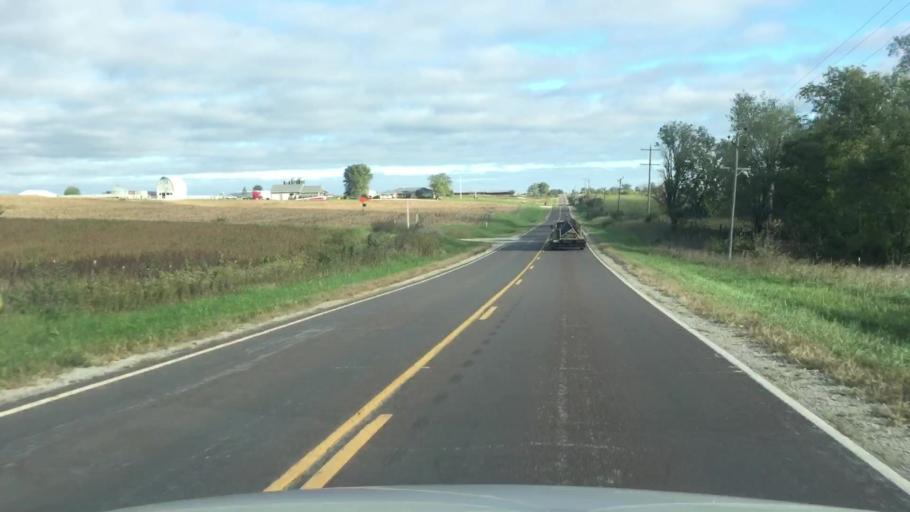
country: US
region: Missouri
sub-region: Howard County
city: New Franklin
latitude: 39.0673
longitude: -92.7460
